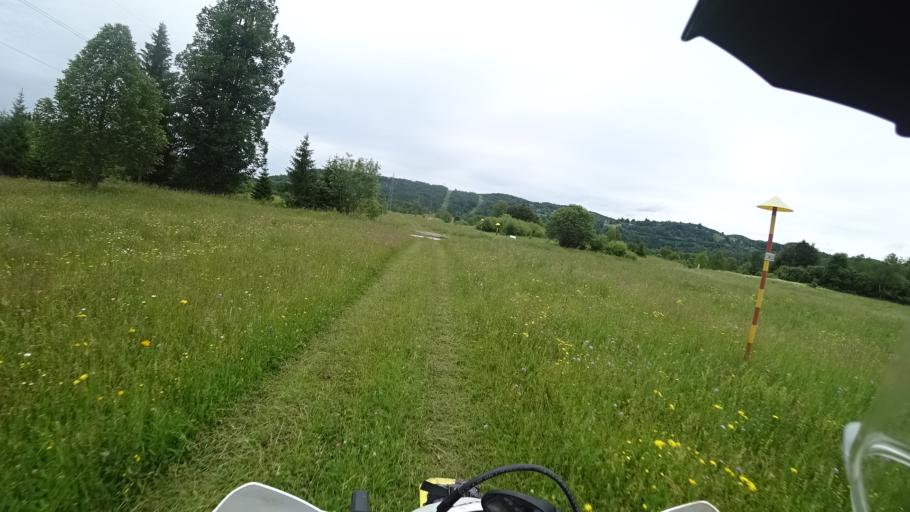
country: HR
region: Primorsko-Goranska
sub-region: Grad Delnice
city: Delnice
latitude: 45.3801
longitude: 14.8760
